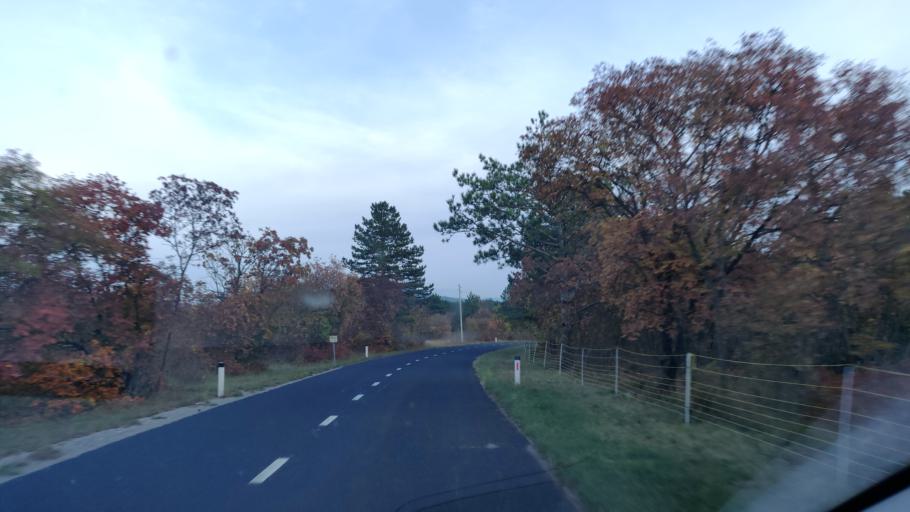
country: SI
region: Sezana
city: Sezana
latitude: 45.7510
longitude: 13.9221
